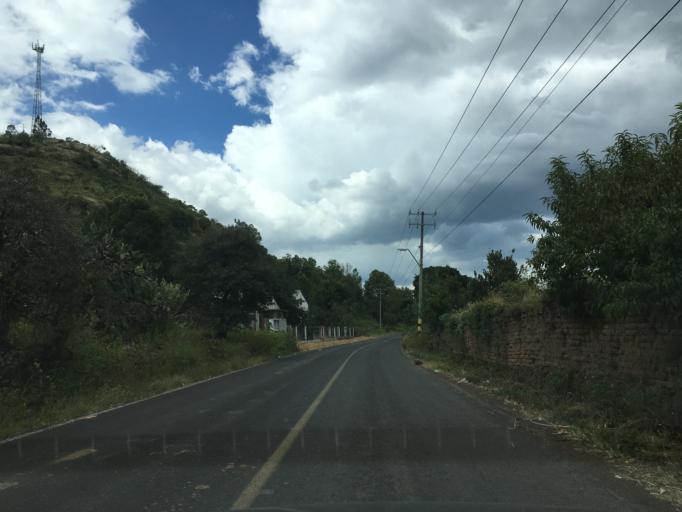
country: MX
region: Michoacan
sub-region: Zacapu
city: Naranja de Tapia
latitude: 19.8186
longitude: -101.7096
